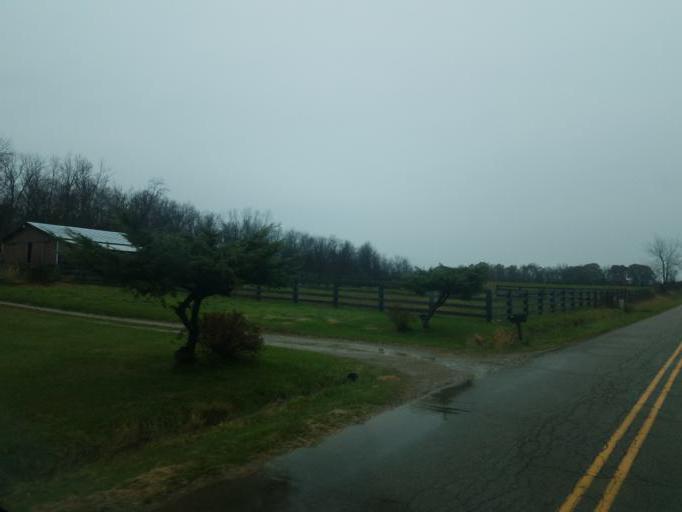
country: US
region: Ohio
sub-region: Knox County
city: Centerburg
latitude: 40.3811
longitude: -82.6172
